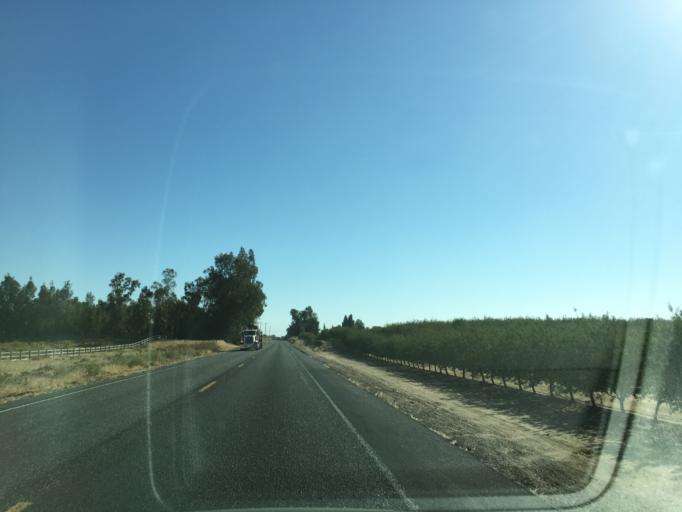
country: US
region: California
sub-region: Madera County
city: Parksdale
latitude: 36.9949
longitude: -119.9979
